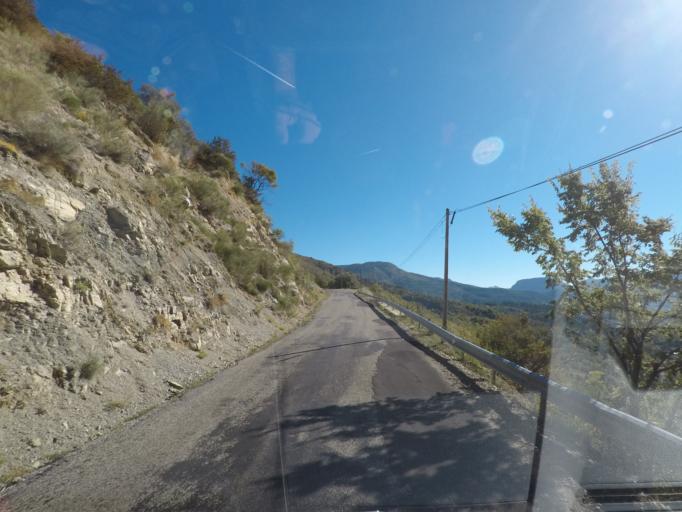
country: FR
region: Rhone-Alpes
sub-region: Departement de la Drome
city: Die
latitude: 44.5084
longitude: 5.3437
